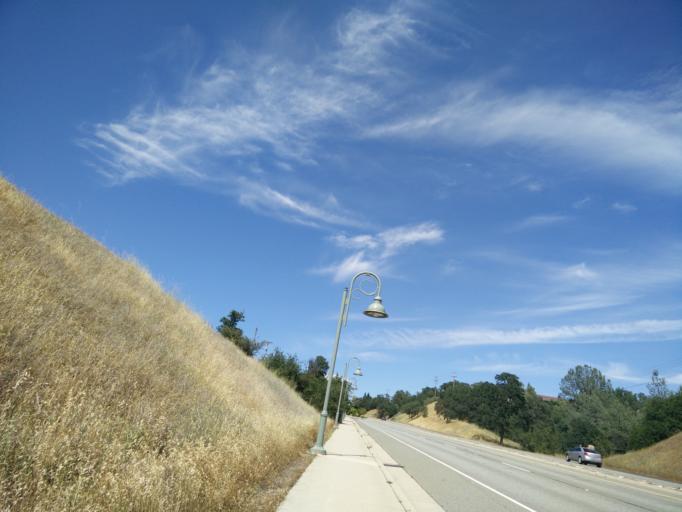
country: US
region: California
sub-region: Shasta County
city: Redding
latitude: 40.6032
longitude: -122.3805
